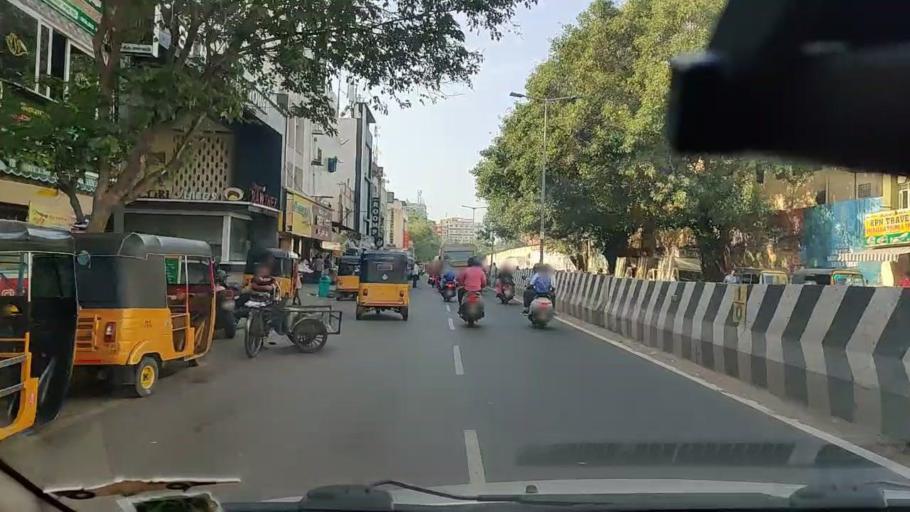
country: IN
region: Tamil Nadu
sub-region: Chennai
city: Chennai
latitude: 13.0844
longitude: 80.2759
